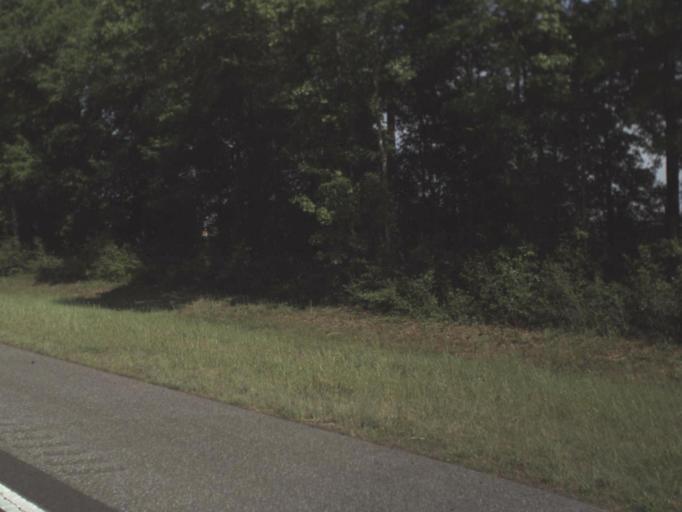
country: US
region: Florida
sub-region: Santa Rosa County
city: East Milton
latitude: 30.6562
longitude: -86.8773
